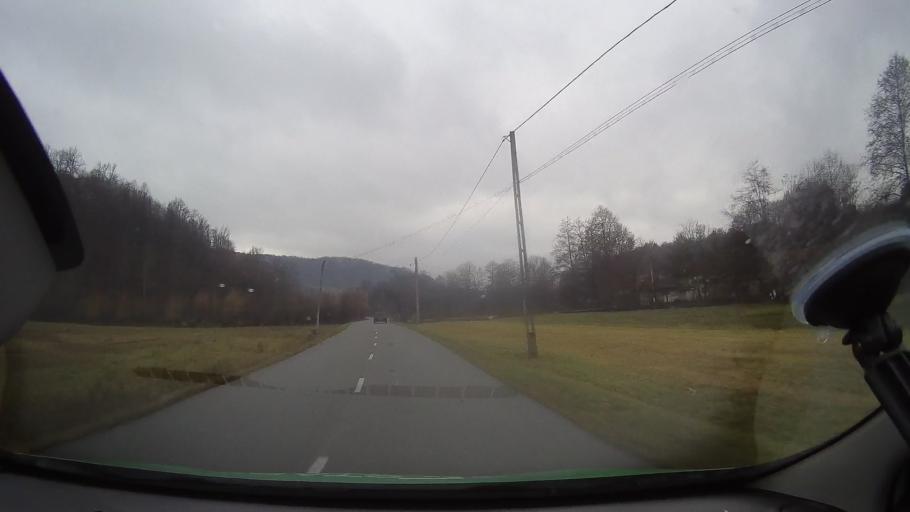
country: RO
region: Hunedoara
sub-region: Comuna Tomesti
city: Tomesti
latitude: 46.2007
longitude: 22.6595
